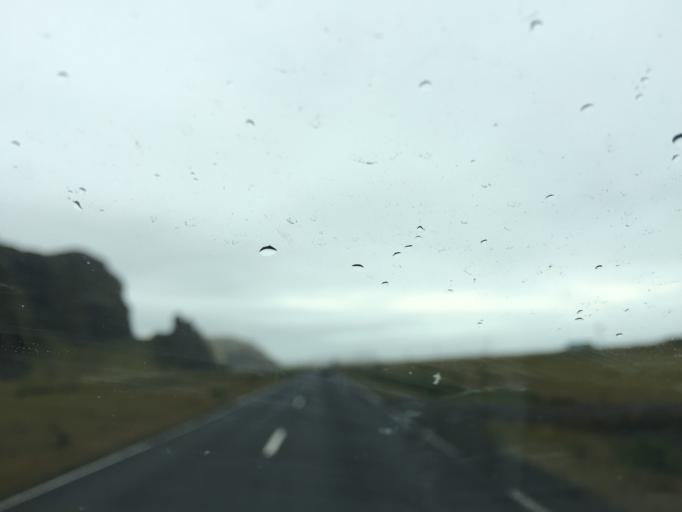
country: IS
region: South
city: Vestmannaeyjar
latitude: 63.4180
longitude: -18.9838
